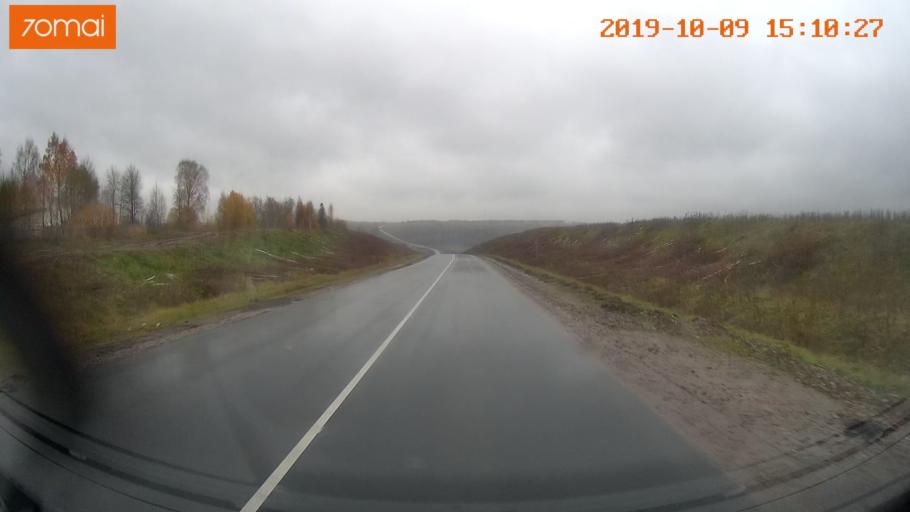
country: RU
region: Kostroma
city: Susanino
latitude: 58.1782
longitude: 41.6408
